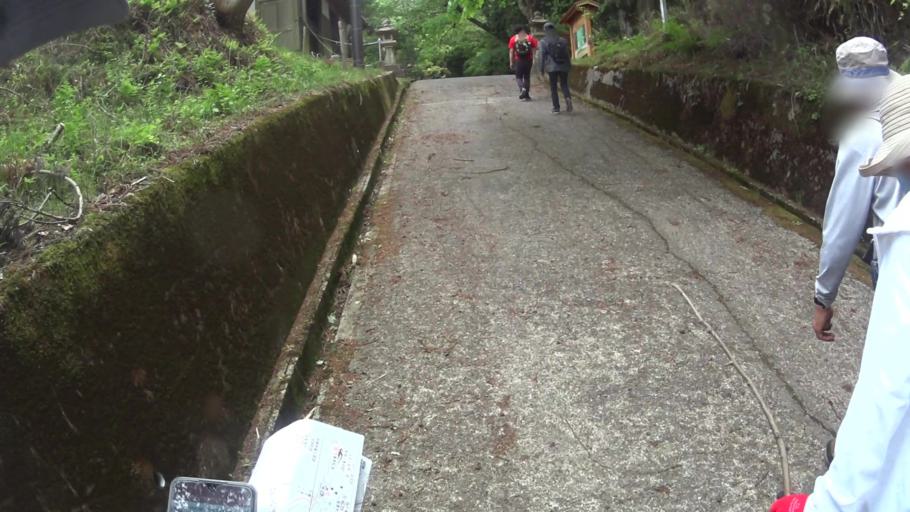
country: JP
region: Nara
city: Yoshino-cho
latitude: 34.3434
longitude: 135.8820
